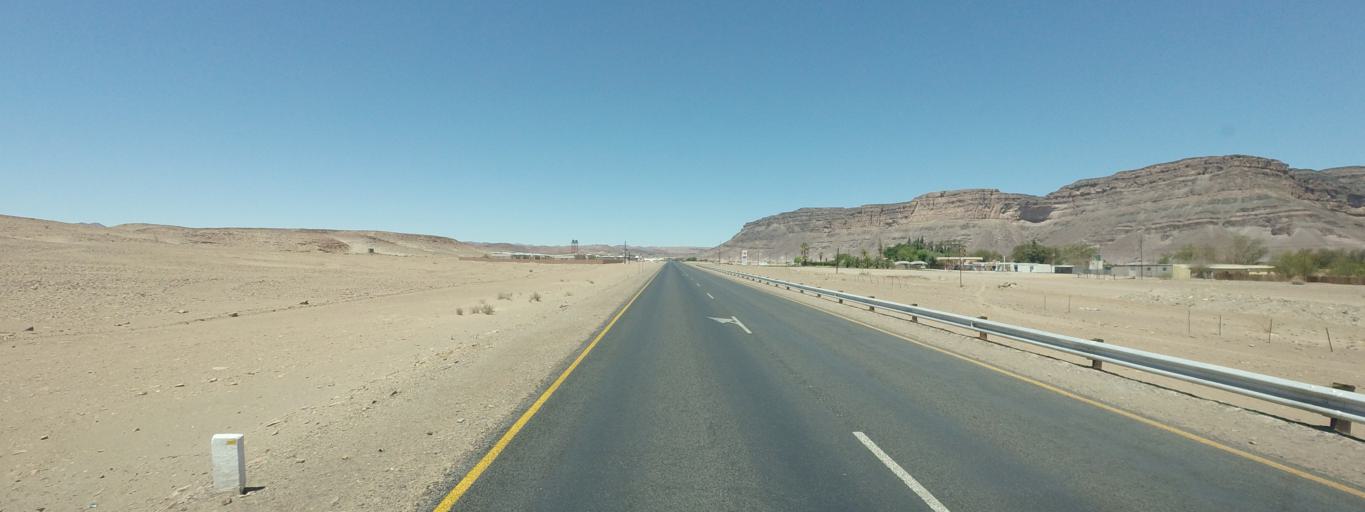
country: ZA
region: Northern Cape
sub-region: Namakwa District Municipality
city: Port Nolloth
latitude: -28.7412
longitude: 17.6176
